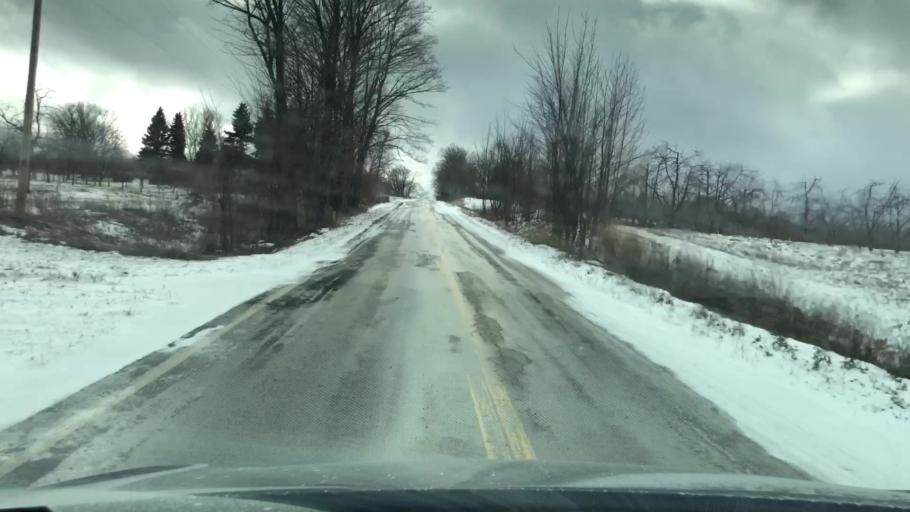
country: US
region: Michigan
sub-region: Antrim County
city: Elk Rapids
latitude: 44.9386
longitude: -85.5156
